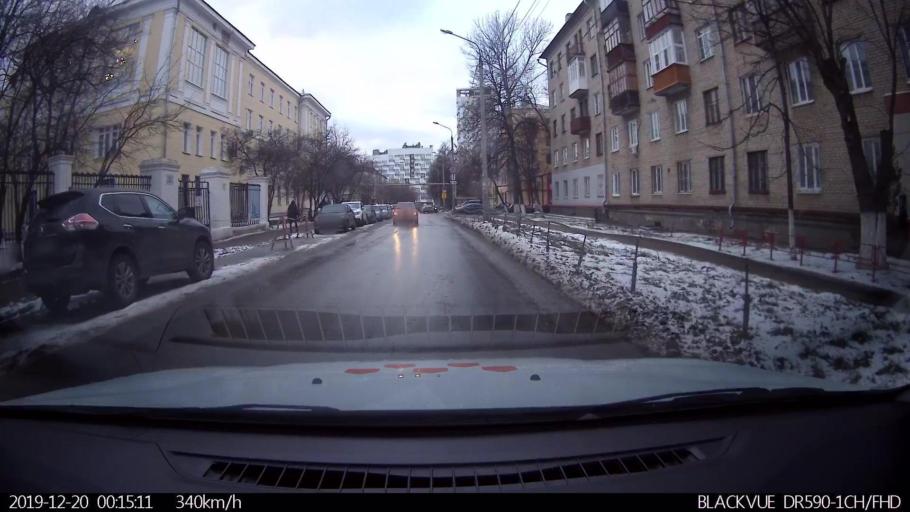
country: RU
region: Jaroslavl
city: Porech'ye-Rybnoye
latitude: 57.0007
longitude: 39.4052
